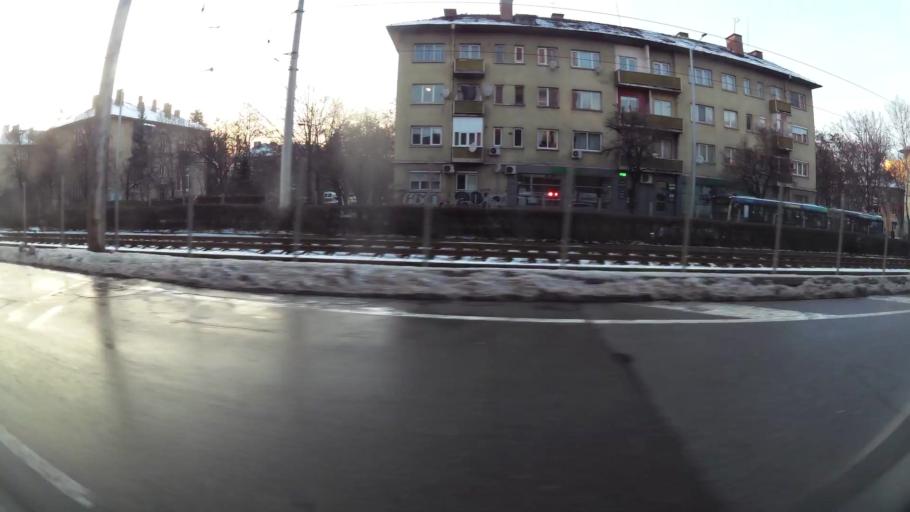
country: BG
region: Sofia-Capital
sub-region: Stolichna Obshtina
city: Sofia
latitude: 42.6895
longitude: 23.3536
